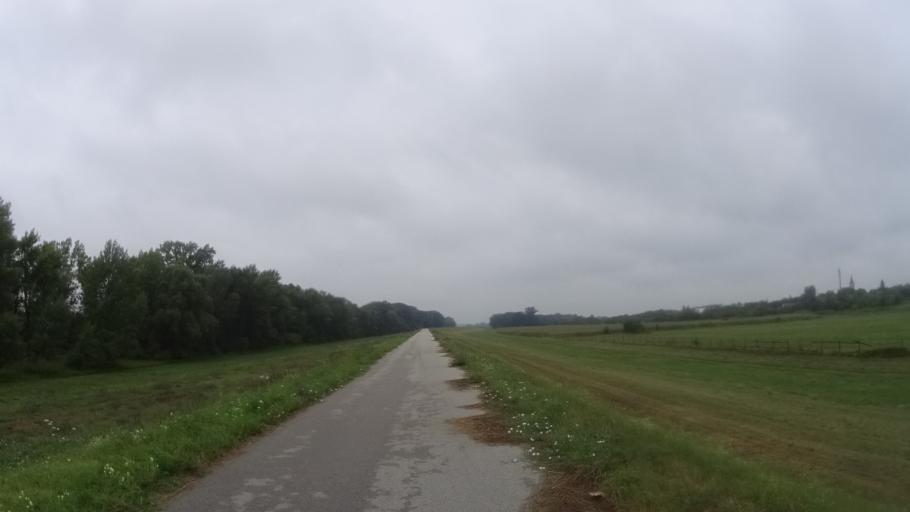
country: HU
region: Komarom-Esztergom
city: Almasfuzito
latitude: 47.7450
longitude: 18.2325
